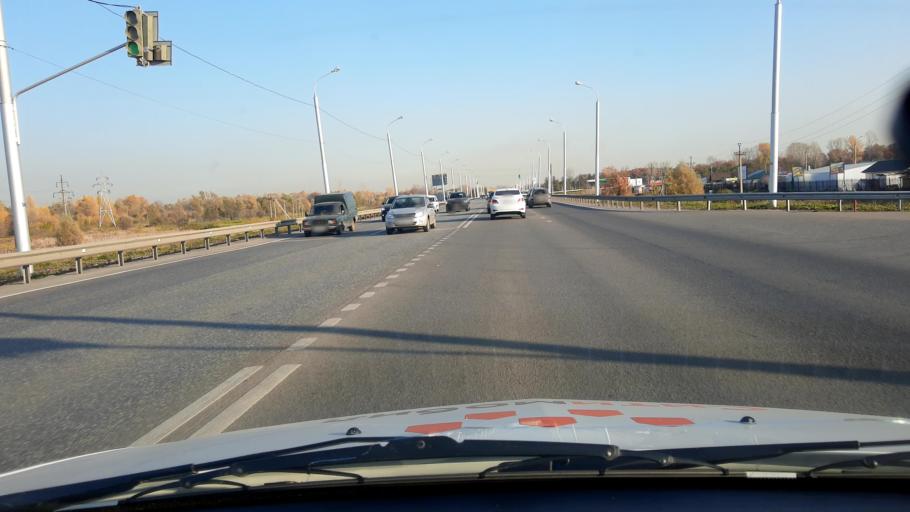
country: RU
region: Bashkortostan
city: Ufa
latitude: 54.8079
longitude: 56.1716
